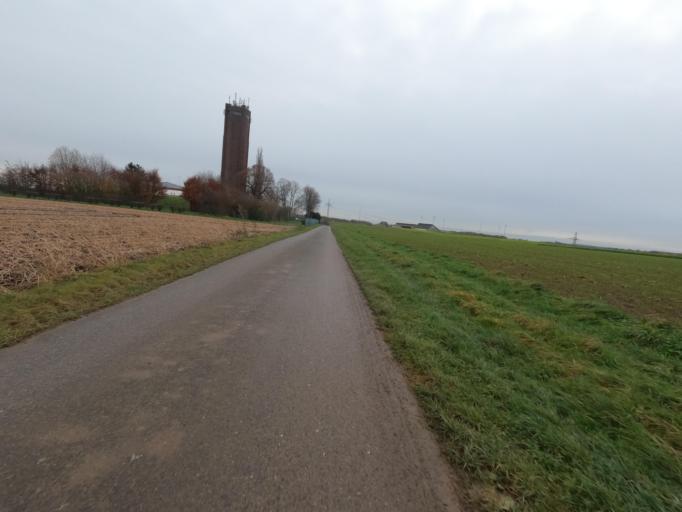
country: DE
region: North Rhine-Westphalia
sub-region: Regierungsbezirk Koln
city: Heinsberg
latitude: 51.0430
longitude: 6.1296
